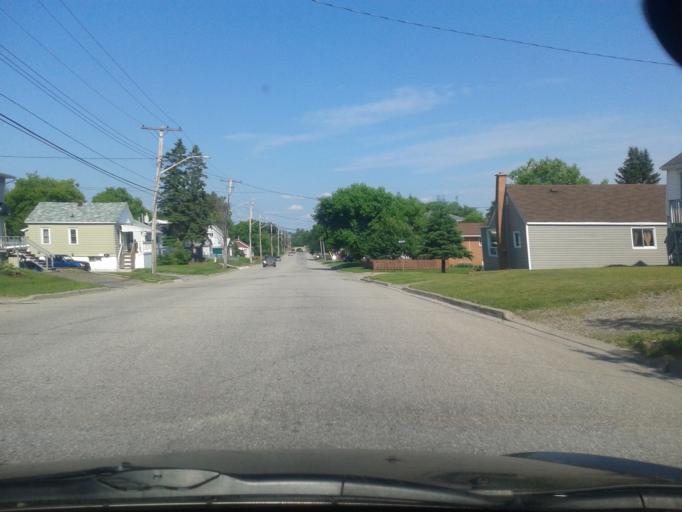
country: CA
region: Ontario
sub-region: Nipissing District
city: North Bay
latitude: 46.3257
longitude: -79.4619
